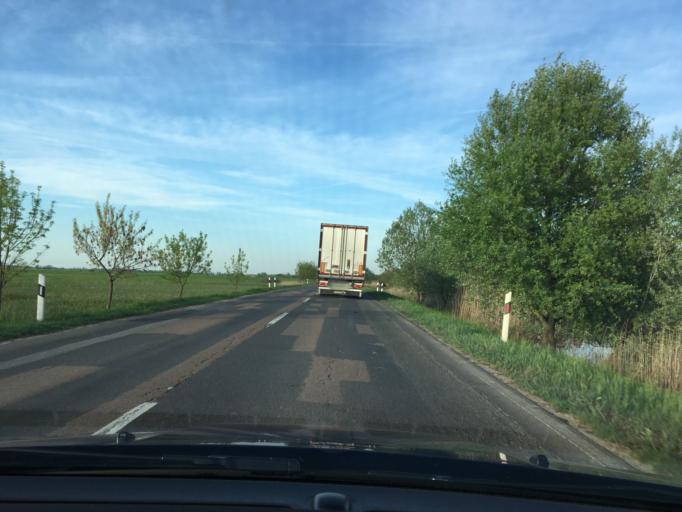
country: HU
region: Hajdu-Bihar
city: Berettyoujfalu
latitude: 47.1621
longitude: 21.5074
